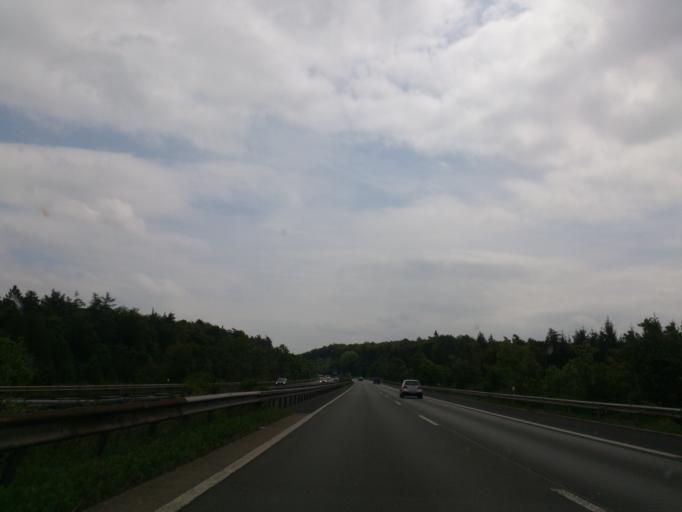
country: DE
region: Hesse
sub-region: Regierungsbezirk Kassel
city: Breuna
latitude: 51.3920
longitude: 9.2147
